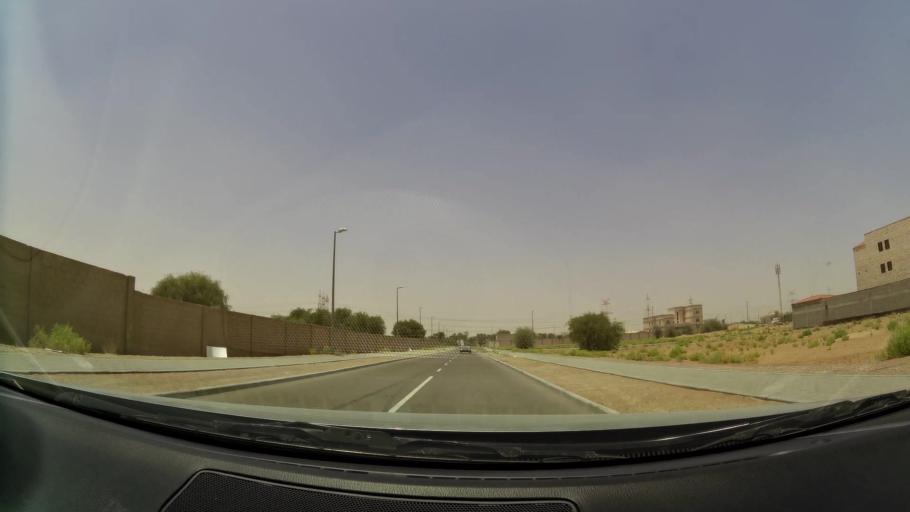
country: OM
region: Al Buraimi
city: Al Buraymi
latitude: 24.2689
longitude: 55.7084
